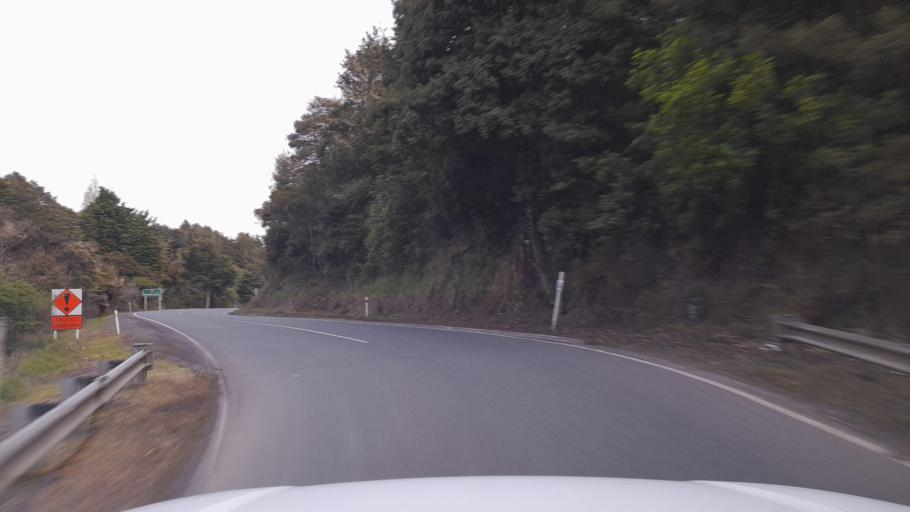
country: NZ
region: Northland
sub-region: Far North District
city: Moerewa
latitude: -35.6235
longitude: 173.8466
